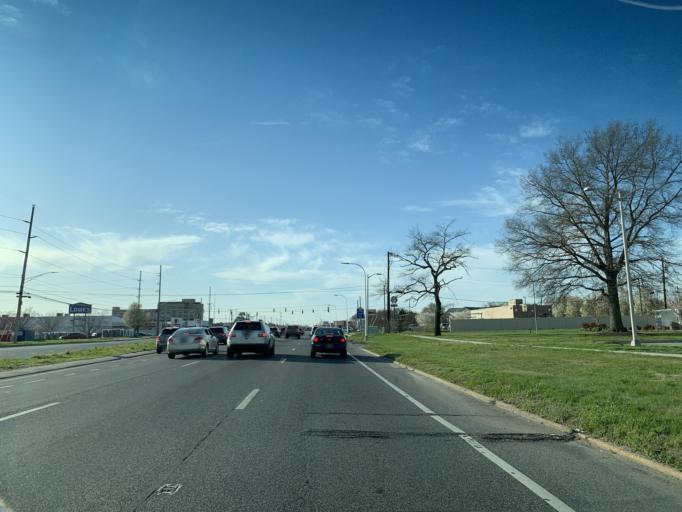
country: US
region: Delaware
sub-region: Kent County
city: Dover
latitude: 39.1932
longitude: -75.5459
